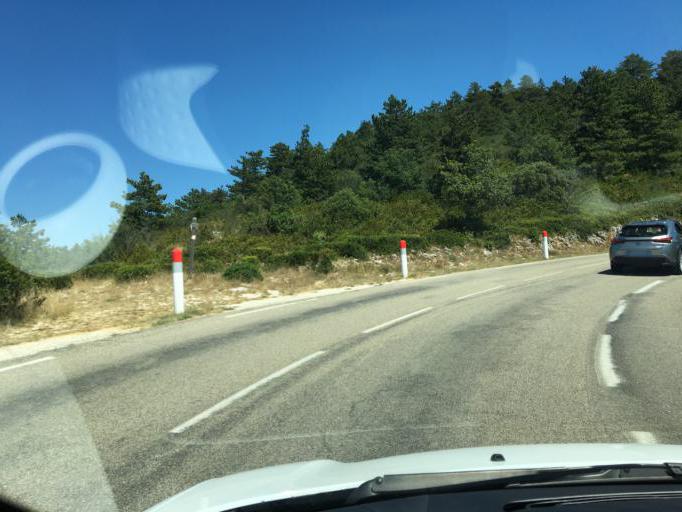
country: FR
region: Provence-Alpes-Cote d'Azur
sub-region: Departement du Vaucluse
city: Bedoin
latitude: 44.1693
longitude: 5.1909
